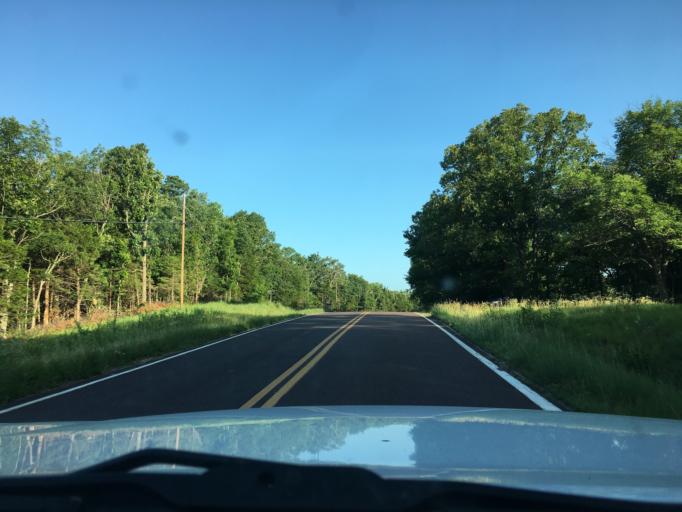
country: US
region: Missouri
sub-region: Gasconade County
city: Owensville
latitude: 38.4483
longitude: -91.6326
